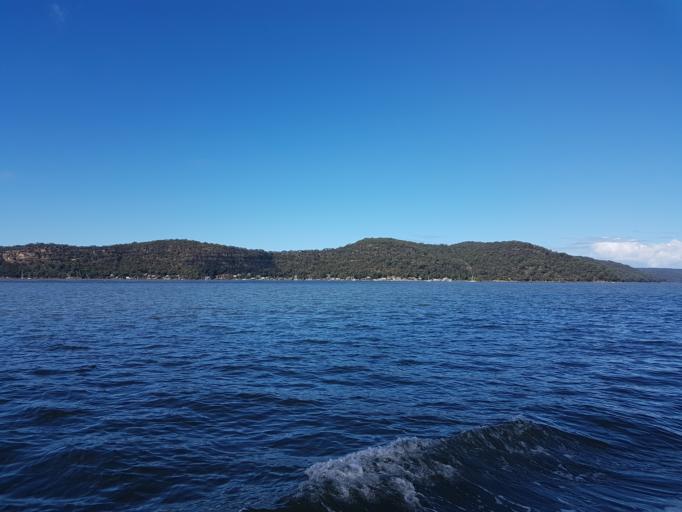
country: AU
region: New South Wales
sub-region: Gosford Shire
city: Umina
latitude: -33.5441
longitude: 151.2329
